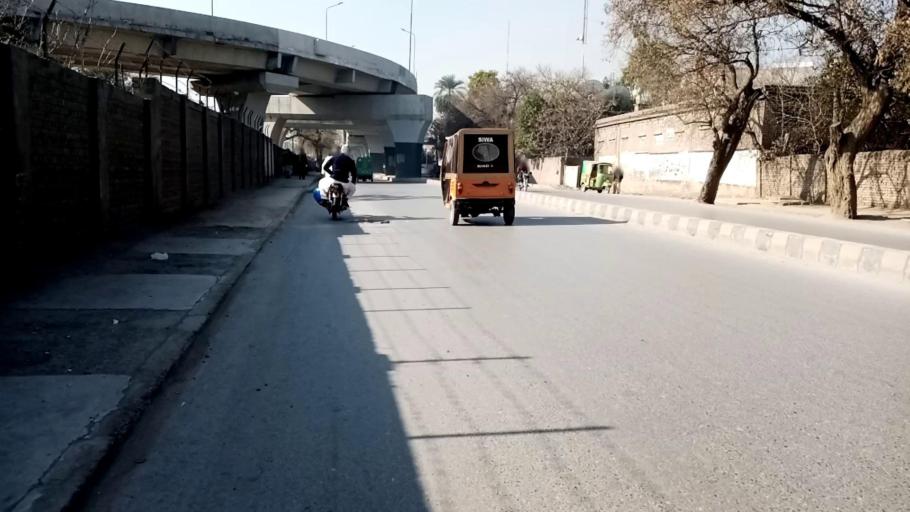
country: PK
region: Khyber Pakhtunkhwa
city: Peshawar
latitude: 34.0045
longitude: 71.5527
